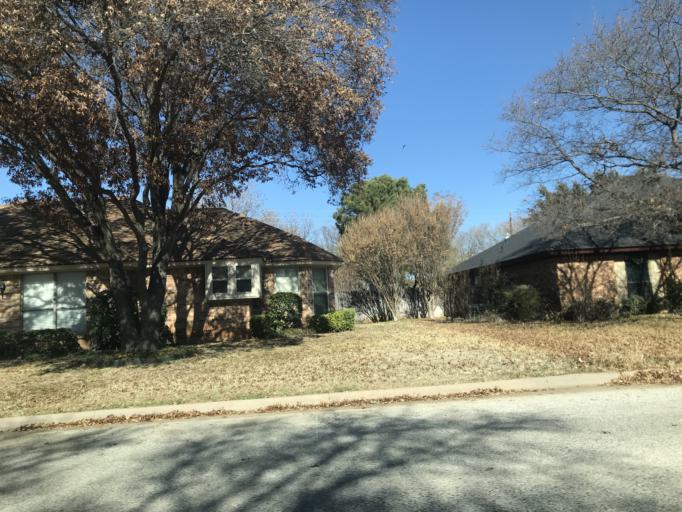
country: US
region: Texas
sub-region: Taylor County
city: Abilene
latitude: 32.3835
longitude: -99.7582
